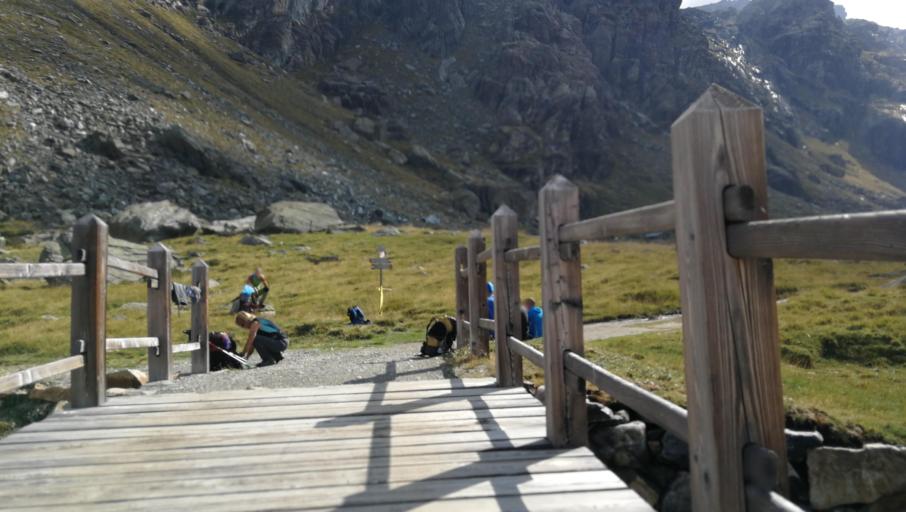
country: CH
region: Grisons
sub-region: Bernina District
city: Poschiavo
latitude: 46.3194
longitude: 9.9607
